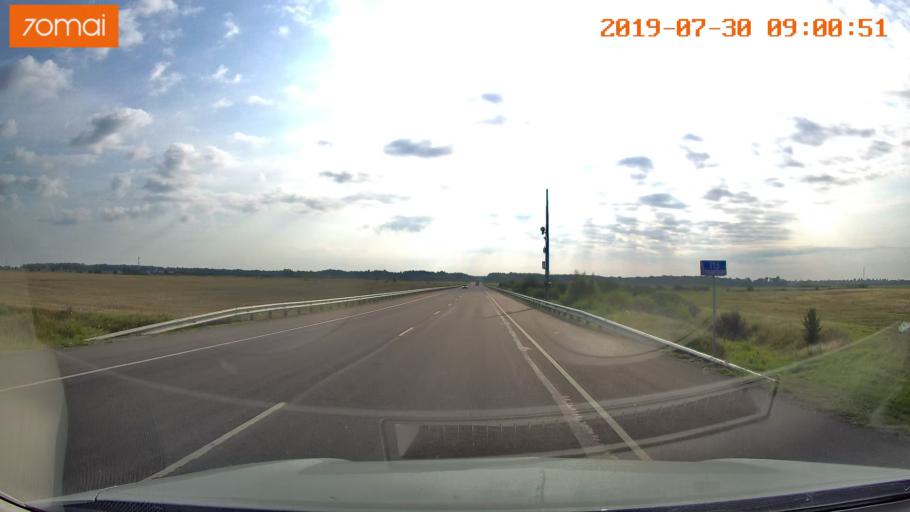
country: RU
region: Kaliningrad
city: Gusev
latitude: 54.6152
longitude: 22.1931
